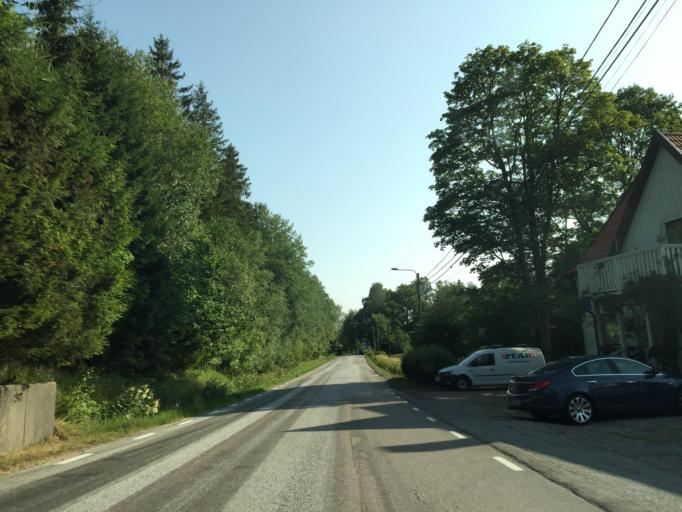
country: SE
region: Vaestra Goetaland
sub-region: Trollhattan
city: Trollhattan
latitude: 58.2973
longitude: 12.2518
